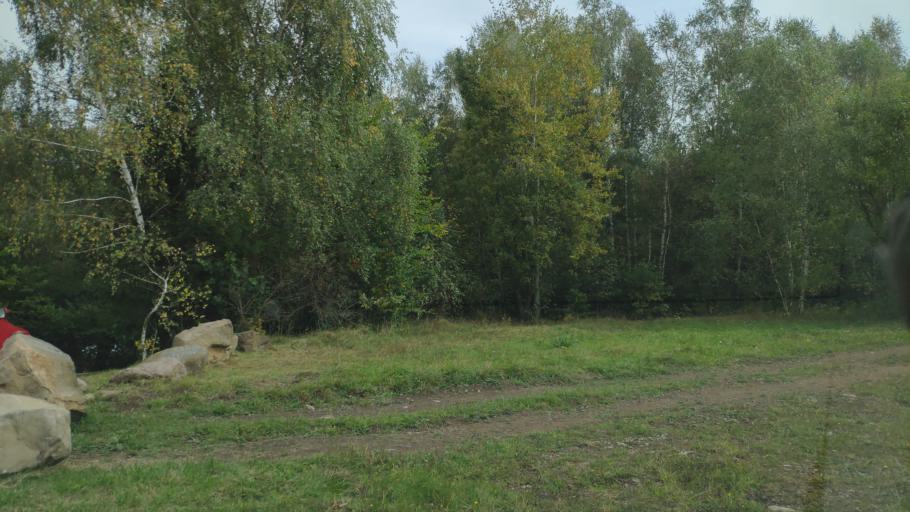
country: SK
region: Presovsky
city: Giraltovce
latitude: 48.9350
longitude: 21.4454
